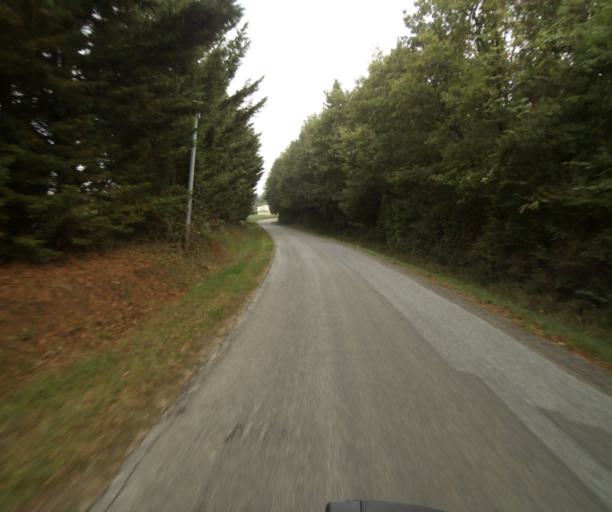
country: FR
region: Midi-Pyrenees
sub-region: Departement du Tarn-et-Garonne
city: Nohic
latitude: 43.9293
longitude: 1.4653
